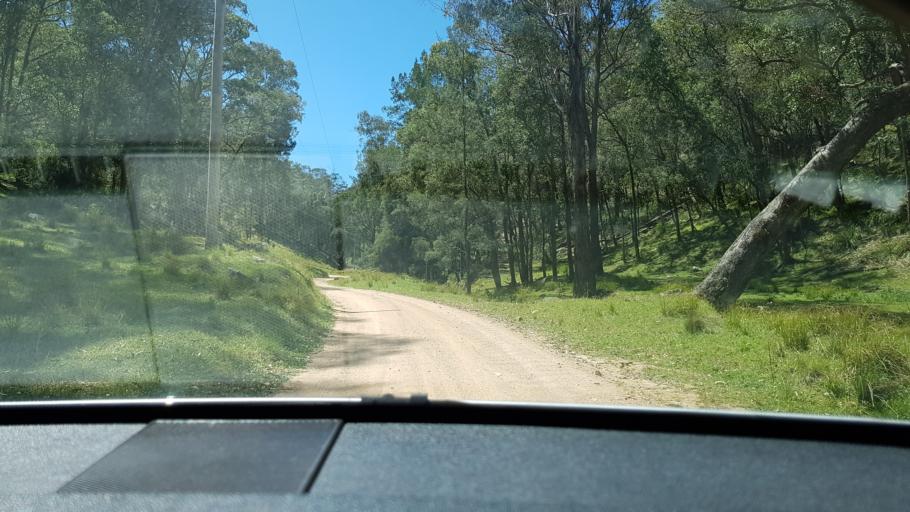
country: AU
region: New South Wales
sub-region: Blue Mountains Municipality
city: Katoomba
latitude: -33.7794
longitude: 150.2329
